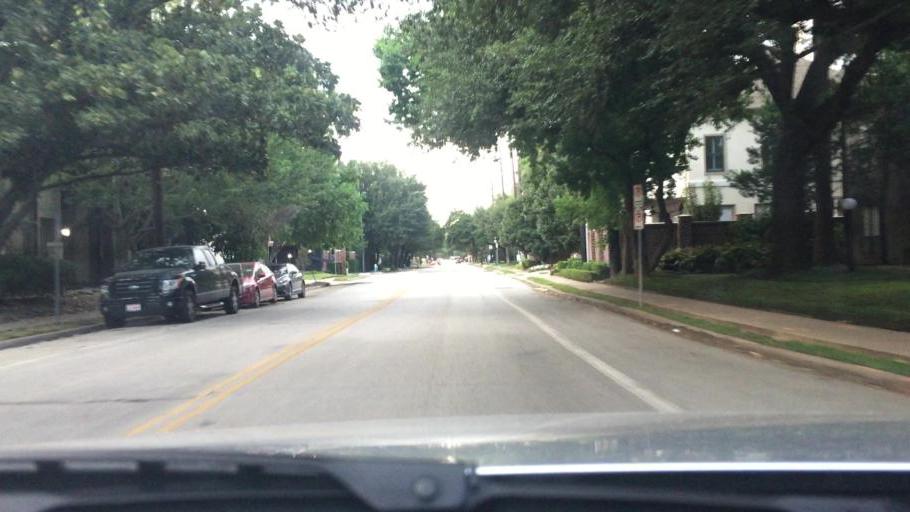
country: US
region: Texas
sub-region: Harris County
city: Hunters Creek Village
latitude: 29.7536
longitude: -95.4796
